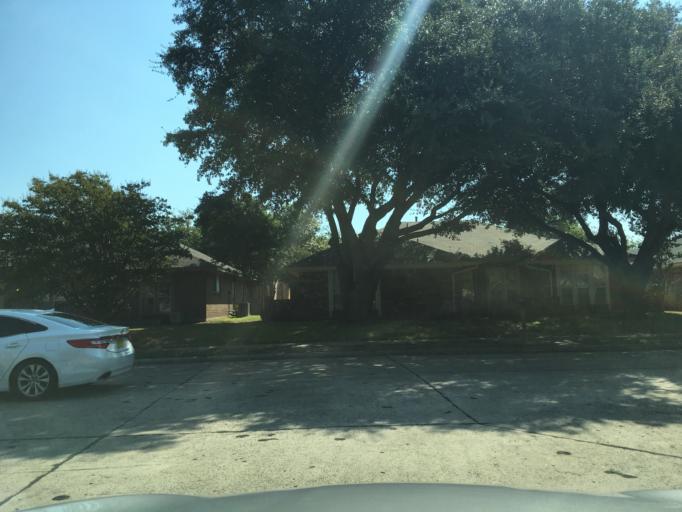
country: US
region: Texas
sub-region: Dallas County
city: Garland
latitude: 32.9326
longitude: -96.6367
